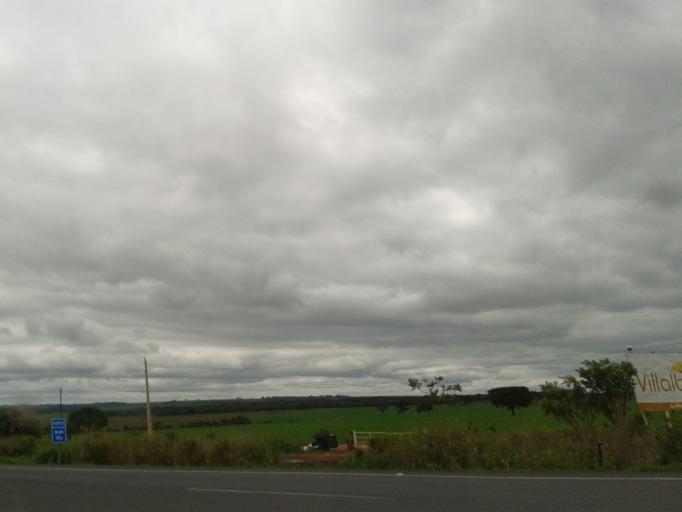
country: BR
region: Minas Gerais
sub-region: Uberlandia
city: Uberlandia
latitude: -19.0163
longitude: -48.2066
